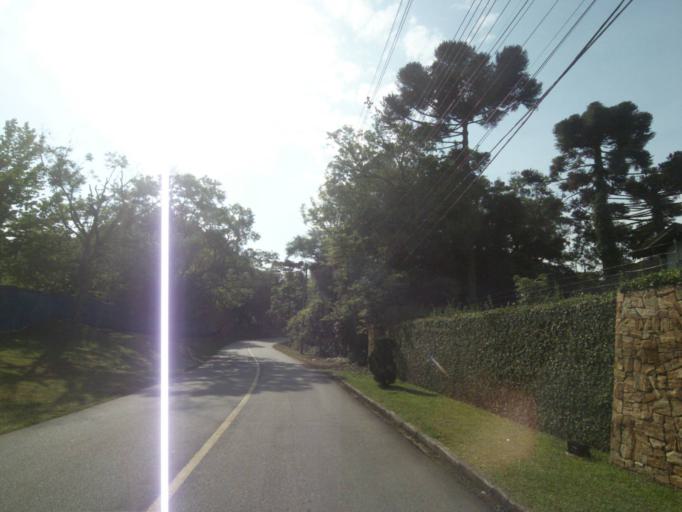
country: BR
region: Parana
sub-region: Curitiba
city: Curitiba
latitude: -25.4177
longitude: -49.3180
